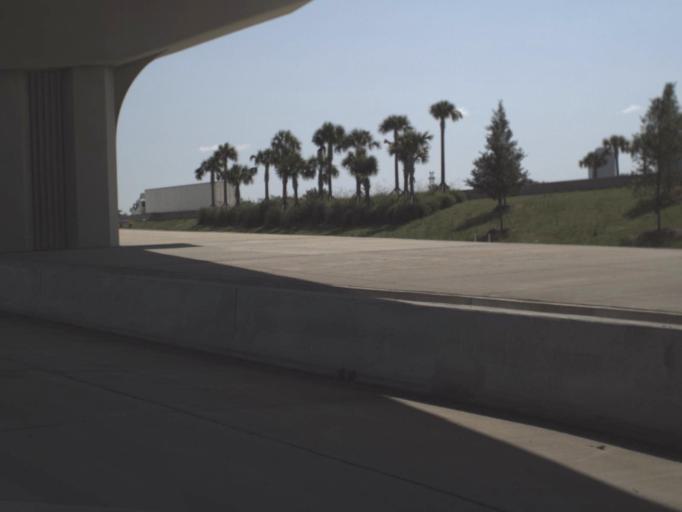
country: US
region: Florida
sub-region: Duval County
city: Jacksonville
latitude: 30.3222
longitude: -81.6810
